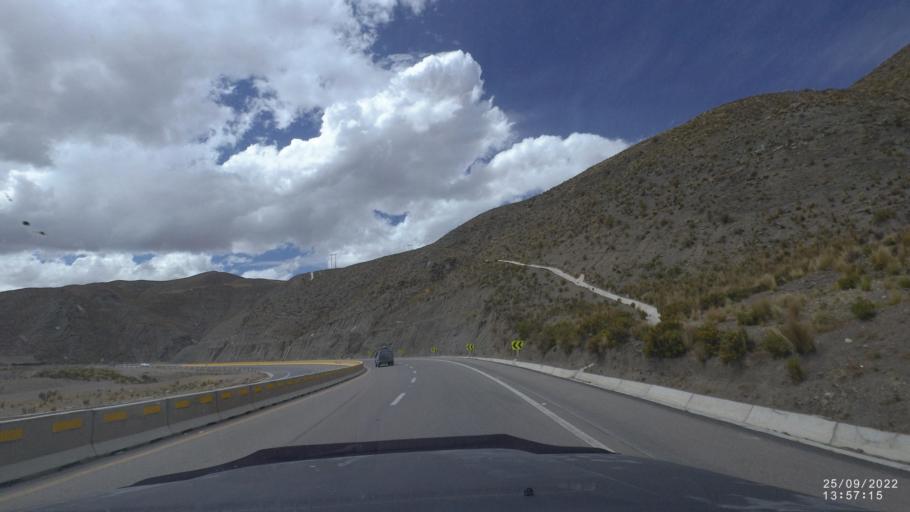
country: BO
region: La Paz
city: Colquiri
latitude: -17.5941
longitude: -66.9590
